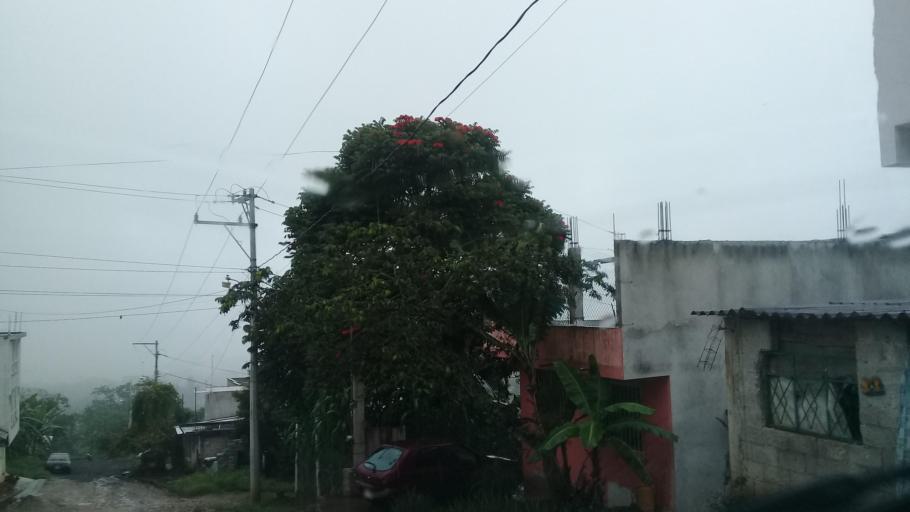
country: MX
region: Veracruz
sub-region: Xalapa
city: Fraccionamiento las Fuentes
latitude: 19.4928
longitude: -96.8810
